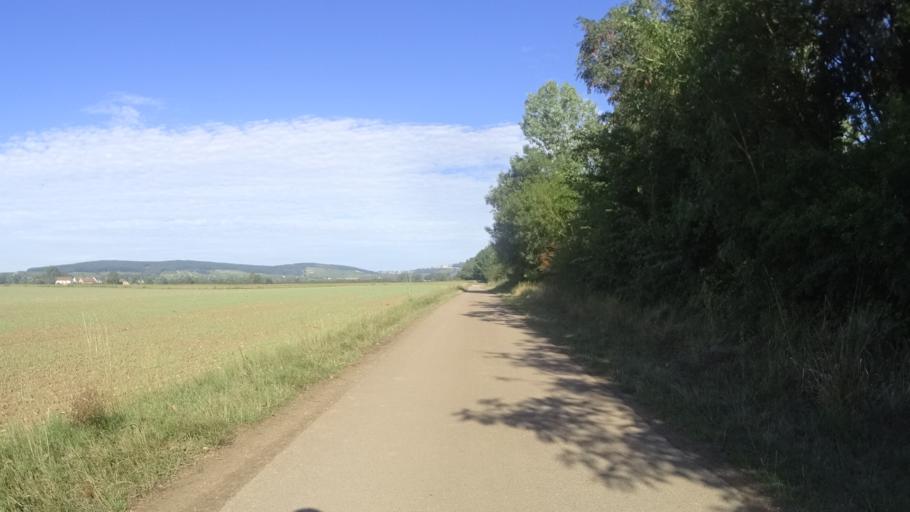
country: FR
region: Bourgogne
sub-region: Departement de la Nievre
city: Pouilly-sur-Loire
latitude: 47.3051
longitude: 2.9016
